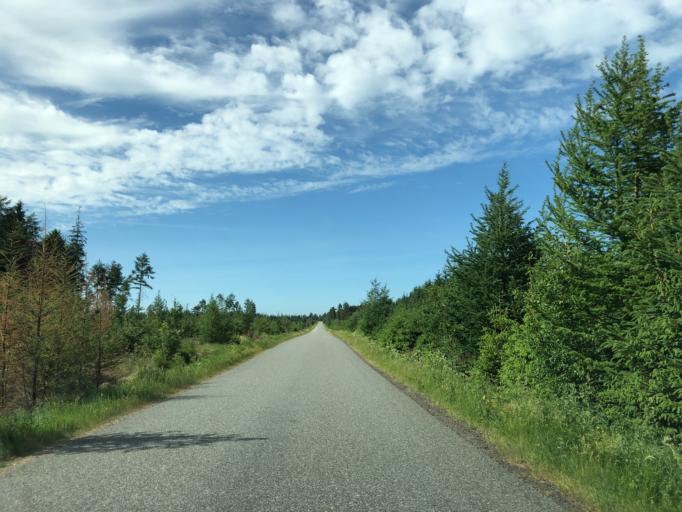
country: DK
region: Central Jutland
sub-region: Herning Kommune
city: Kibaek
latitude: 56.0557
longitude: 8.9229
